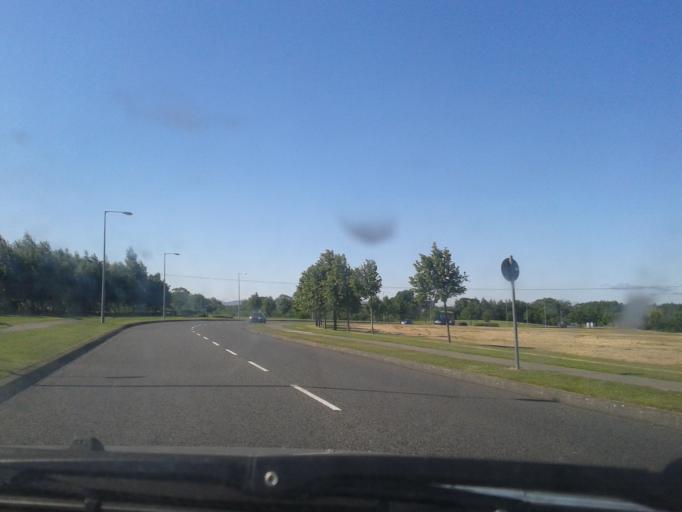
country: IE
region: Leinster
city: Hartstown
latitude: 53.4182
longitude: -6.4180
